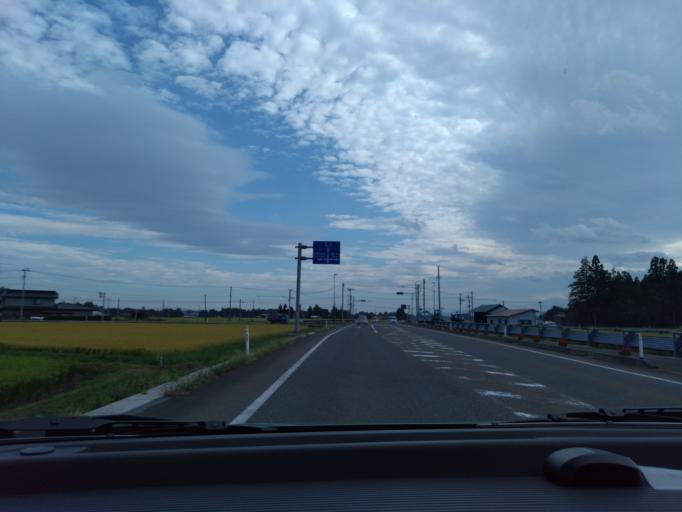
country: JP
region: Iwate
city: Hanamaki
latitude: 39.3640
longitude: 141.0565
